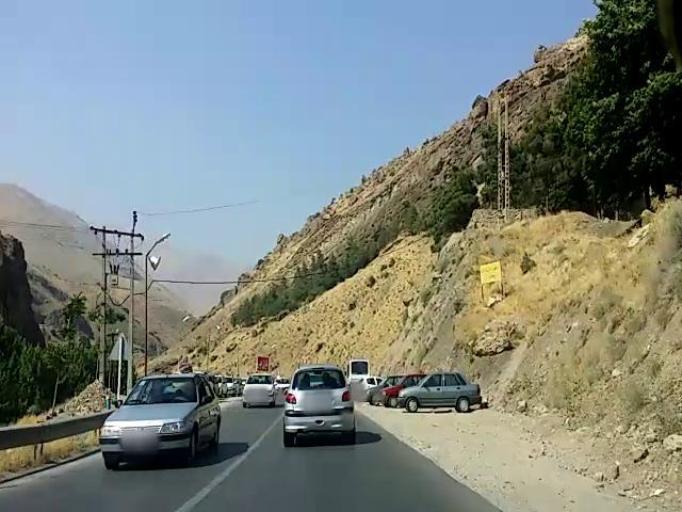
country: IR
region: Alborz
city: Karaj
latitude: 35.9172
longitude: 51.0493
